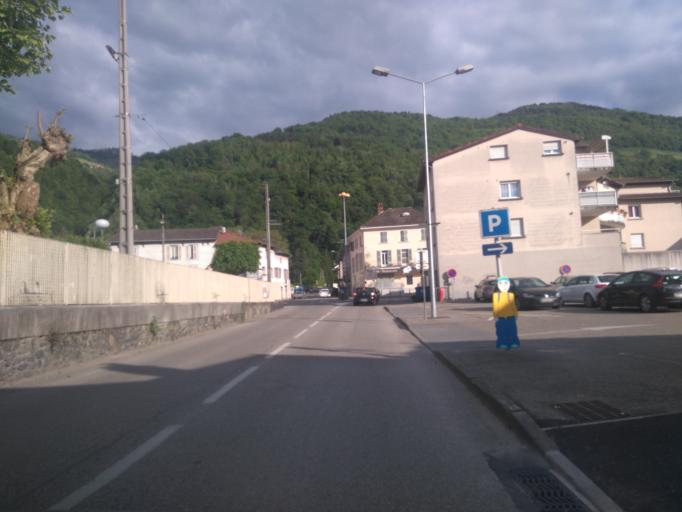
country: FR
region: Rhone-Alpes
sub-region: Departement de l'Isere
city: Villard-Bonnot
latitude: 45.2346
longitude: 5.8819
